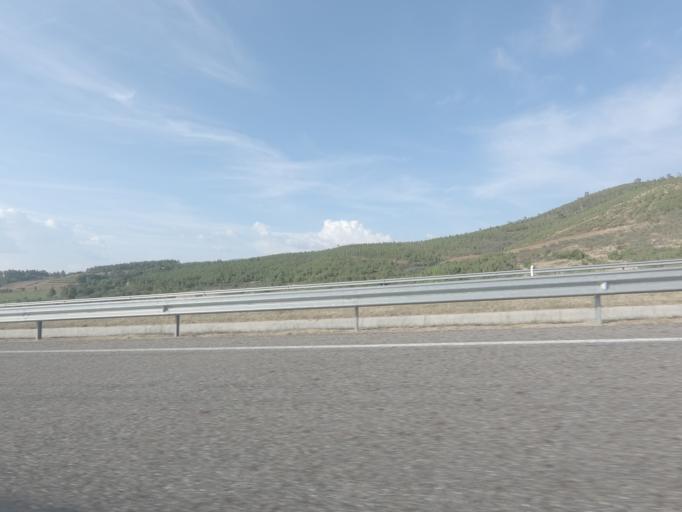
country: ES
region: Galicia
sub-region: Provincia de Ourense
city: Oimbra
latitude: 41.8651
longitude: -7.4297
